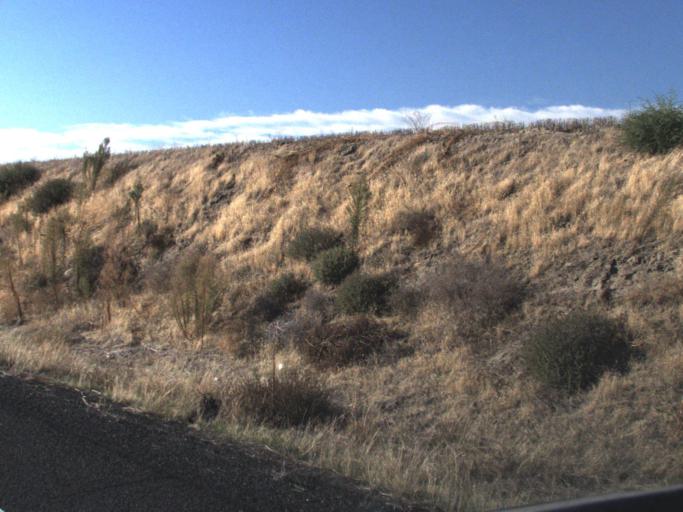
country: US
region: Washington
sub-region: Walla Walla County
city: Garrett
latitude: 46.2965
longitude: -118.5687
